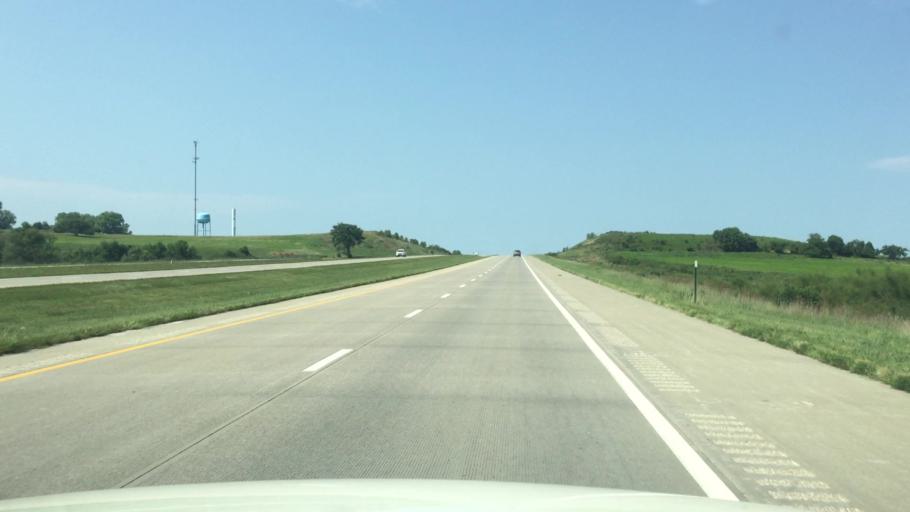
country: US
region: Kansas
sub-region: Linn County
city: Pleasanton
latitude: 38.1016
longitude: -94.7133
